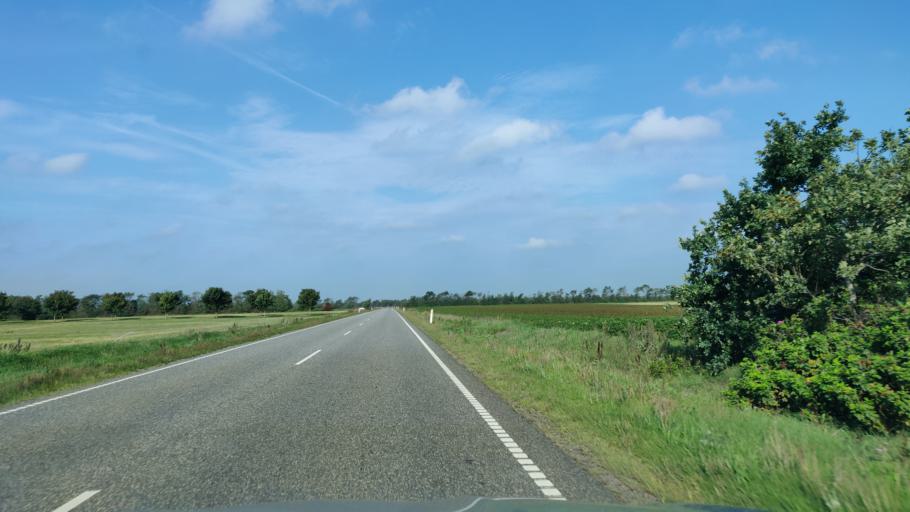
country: DK
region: Central Jutland
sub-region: Herning Kommune
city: Sunds
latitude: 56.2618
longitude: 9.0273
